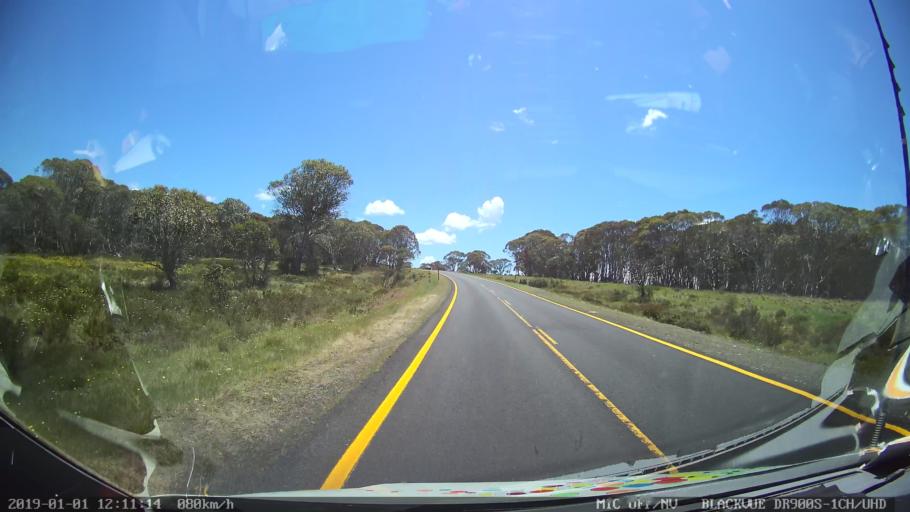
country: AU
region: New South Wales
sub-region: Tumut Shire
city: Tumut
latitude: -35.7863
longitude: 148.5070
